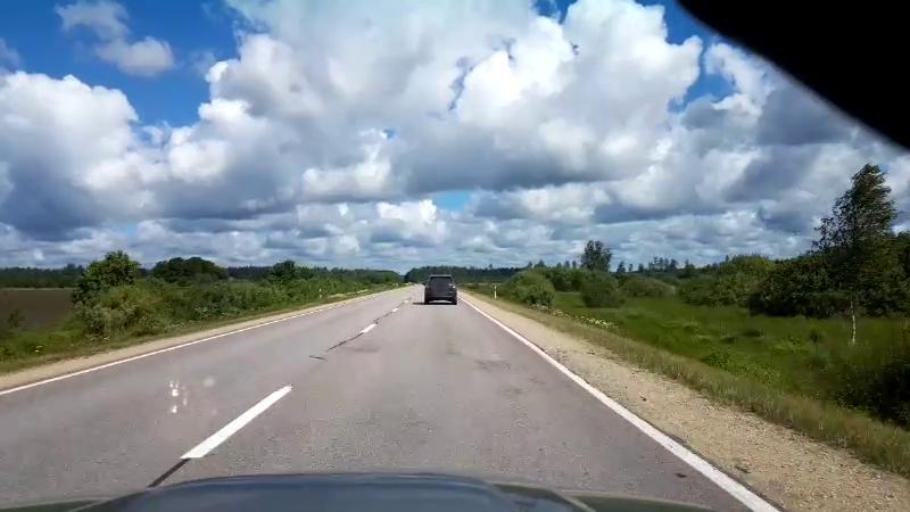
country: LV
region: Salaspils
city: Salaspils
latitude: 56.8800
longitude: 24.4077
